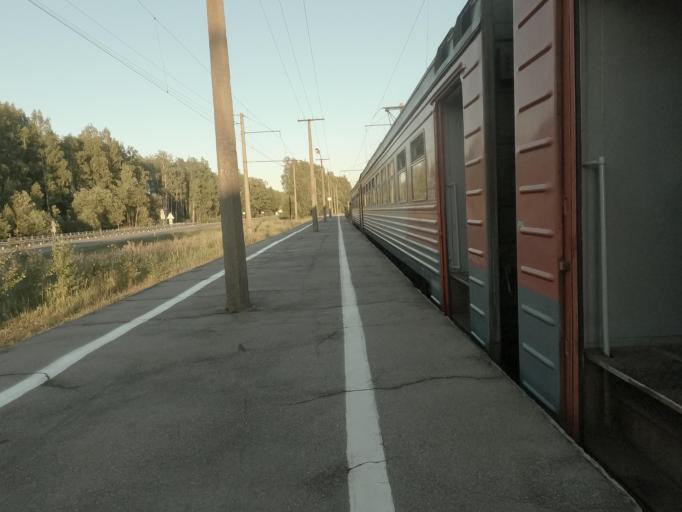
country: RU
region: Leningrad
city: Kirovsk
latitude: 59.8548
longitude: 31.0154
